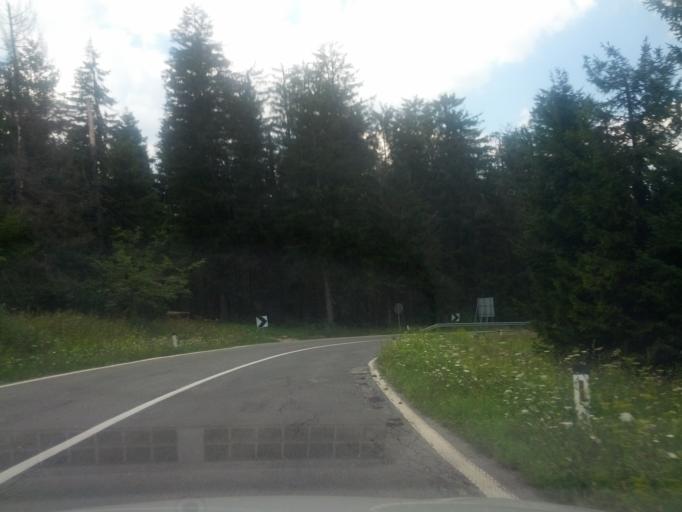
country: SI
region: Postojna
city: Postojna
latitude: 45.7982
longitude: 14.2357
